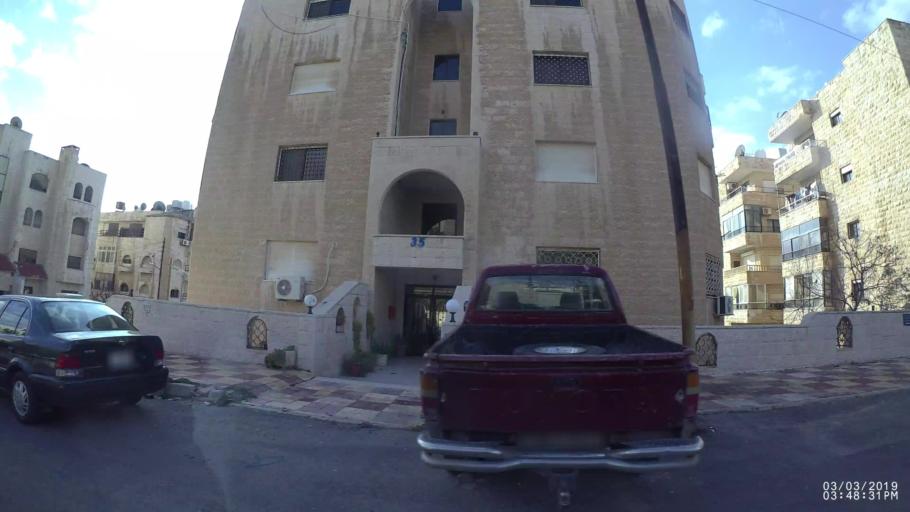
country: JO
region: Amman
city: Al Jubayhah
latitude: 31.9843
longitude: 35.8756
